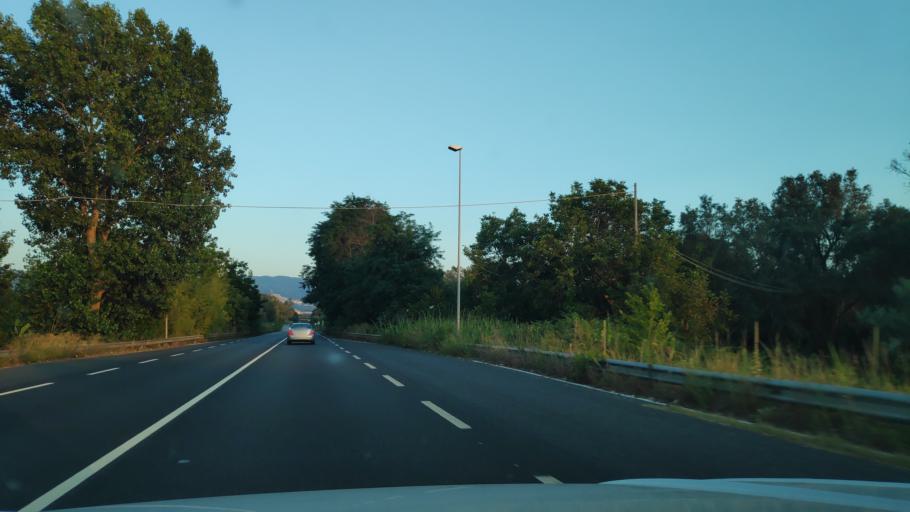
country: IT
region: Calabria
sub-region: Provincia di Reggio Calabria
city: Melicucco
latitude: 38.4285
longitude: 16.0560
